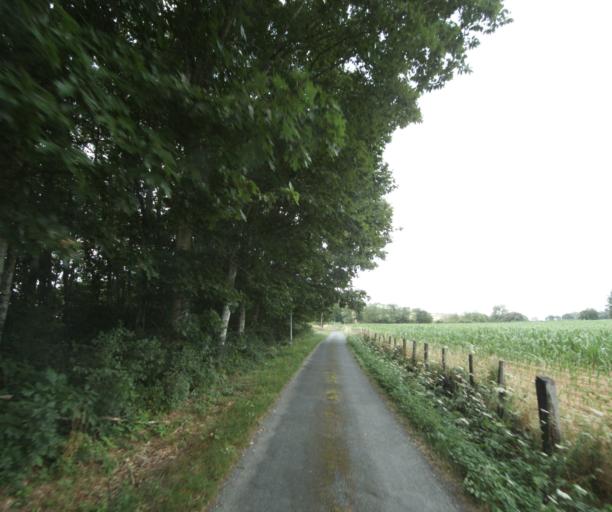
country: FR
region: Bourgogne
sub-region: Departement de Saone-et-Loire
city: Gueugnon
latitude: 46.5890
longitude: 4.0209
